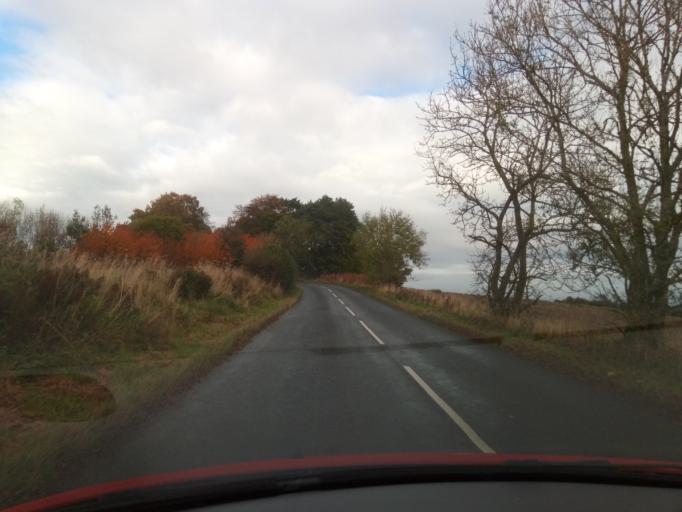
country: GB
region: Scotland
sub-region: The Scottish Borders
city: Newtown St Boswells
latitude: 55.5505
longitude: -2.7057
